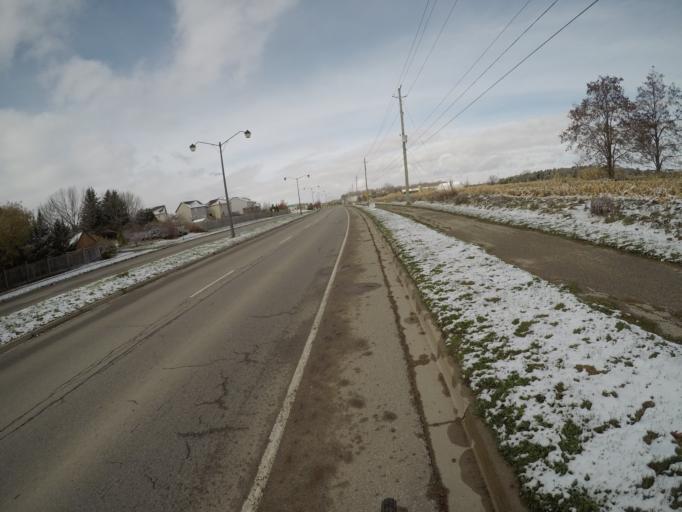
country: CA
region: Ontario
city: Waterloo
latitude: 43.5144
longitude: -80.4987
